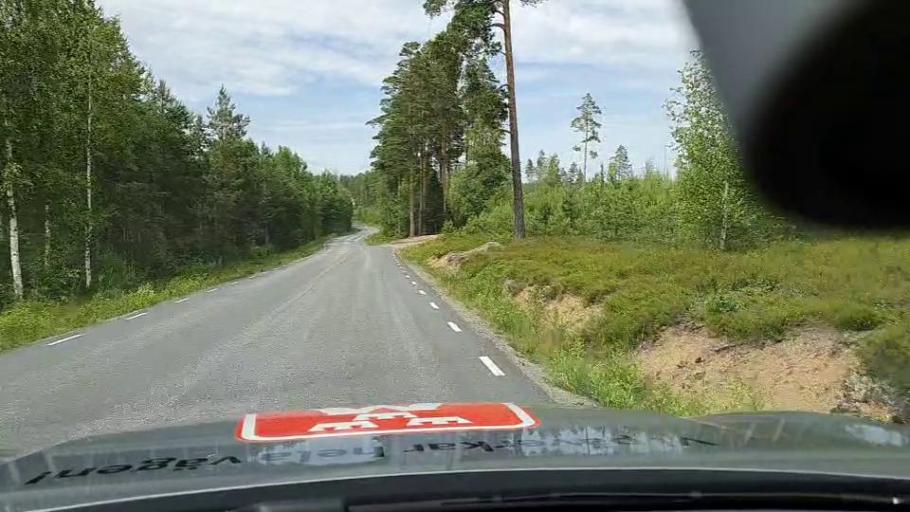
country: SE
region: Soedermanland
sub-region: Eskilstuna Kommun
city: Arla
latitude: 59.2439
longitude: 16.7185
